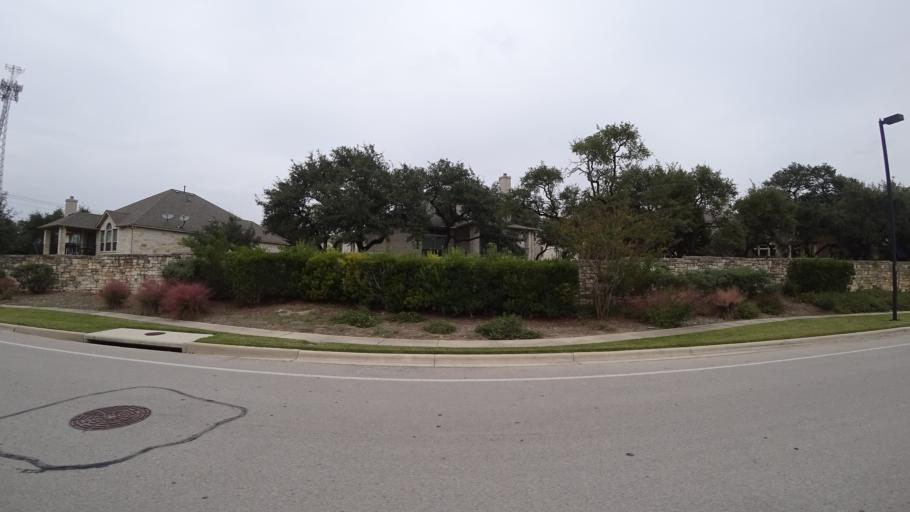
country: US
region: Texas
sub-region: Travis County
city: Shady Hollow
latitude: 30.2003
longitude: -97.9187
